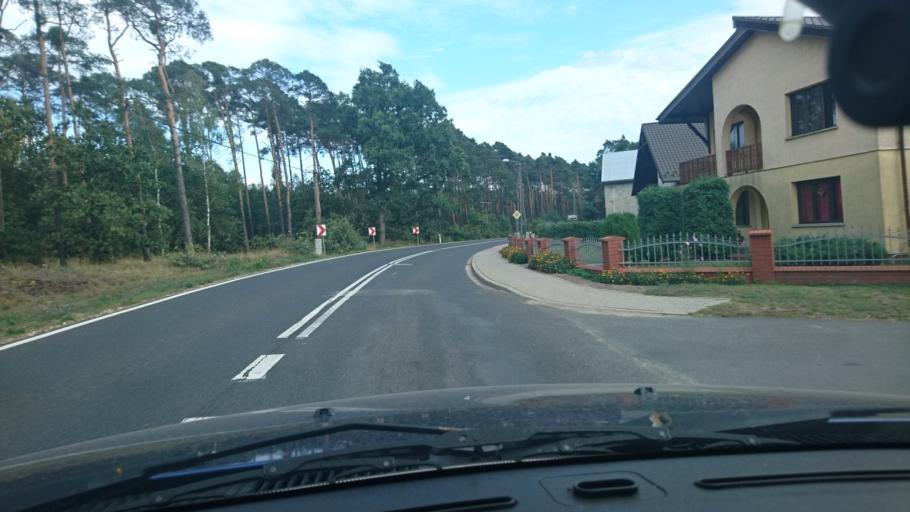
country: PL
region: Greater Poland Voivodeship
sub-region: Powiat ostrowski
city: Jankow Przygodzki
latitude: 51.5016
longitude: 17.7759
